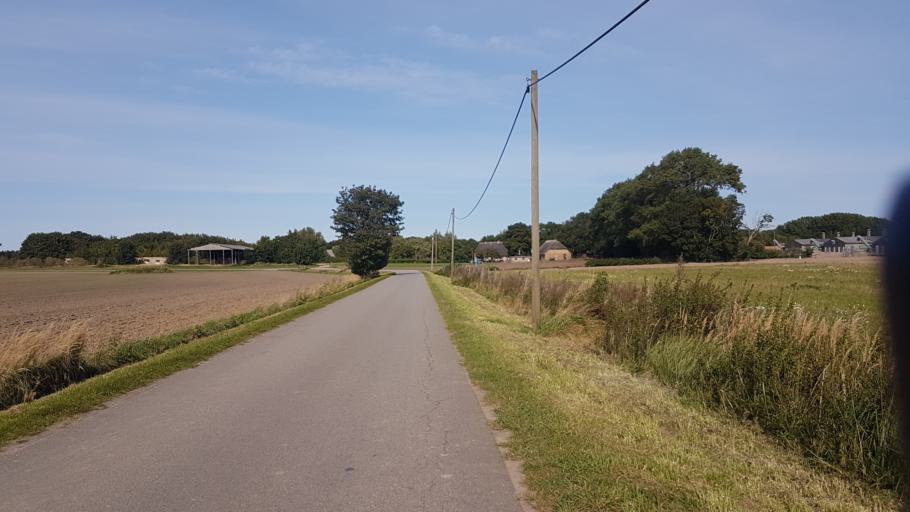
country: DE
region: Mecklenburg-Vorpommern
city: Gingst
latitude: 54.4330
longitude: 13.2238
